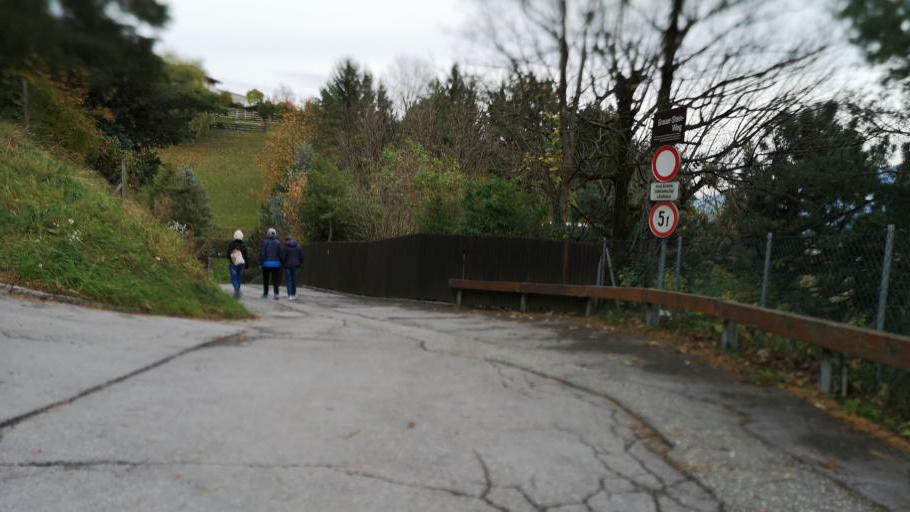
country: AT
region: Tyrol
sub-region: Innsbruck Stadt
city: Innsbruck
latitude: 47.2655
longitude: 11.3655
